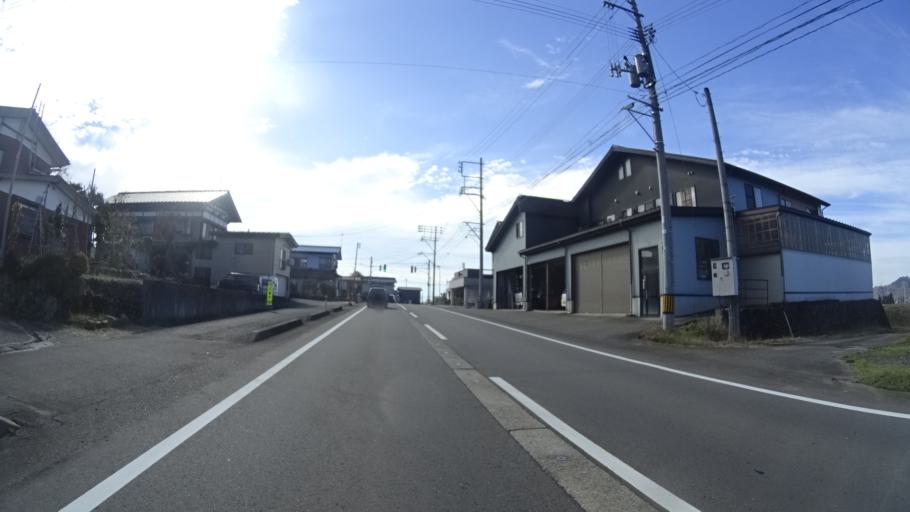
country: JP
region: Niigata
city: Ojiya
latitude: 37.2424
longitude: 138.9811
